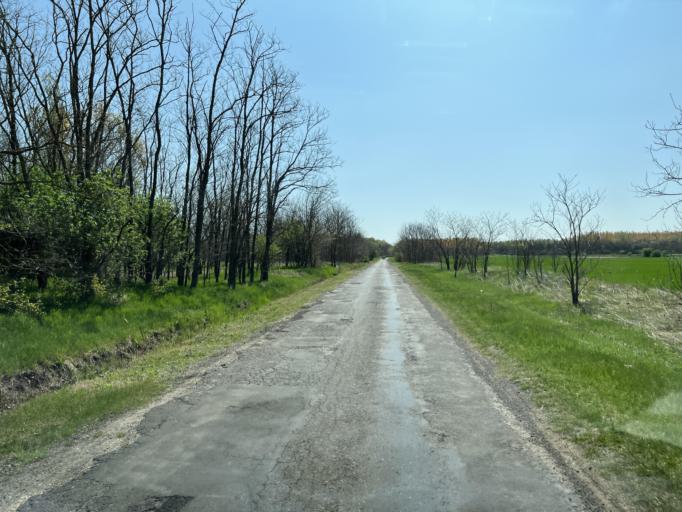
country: HU
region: Pest
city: Ujhartyan
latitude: 47.1714
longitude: 19.3729
